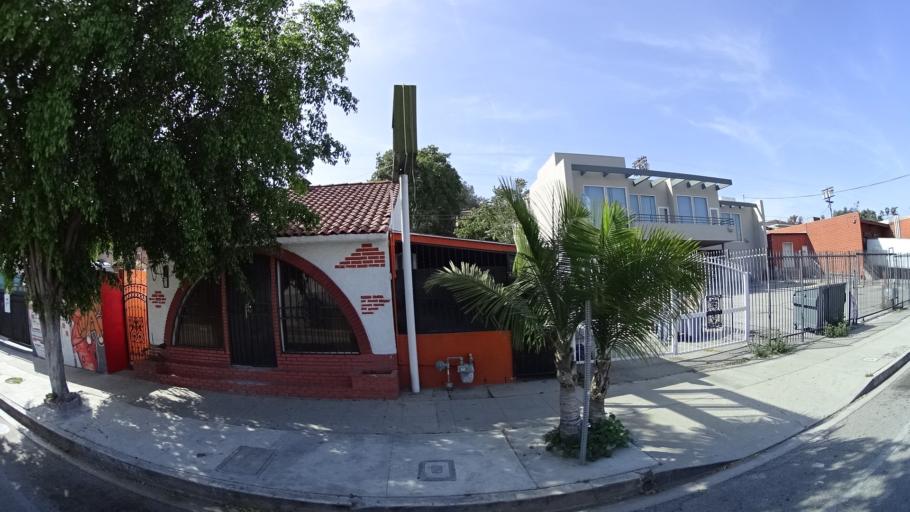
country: US
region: California
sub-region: Los Angeles County
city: Belvedere
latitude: 34.0726
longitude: -118.1737
